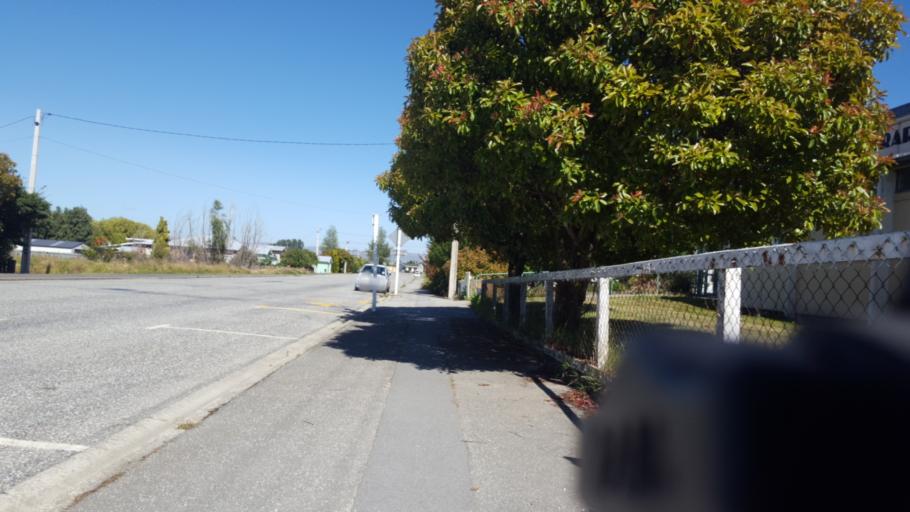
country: NZ
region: Otago
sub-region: Dunedin City
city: Dunedin
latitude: -45.1256
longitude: 170.0987
